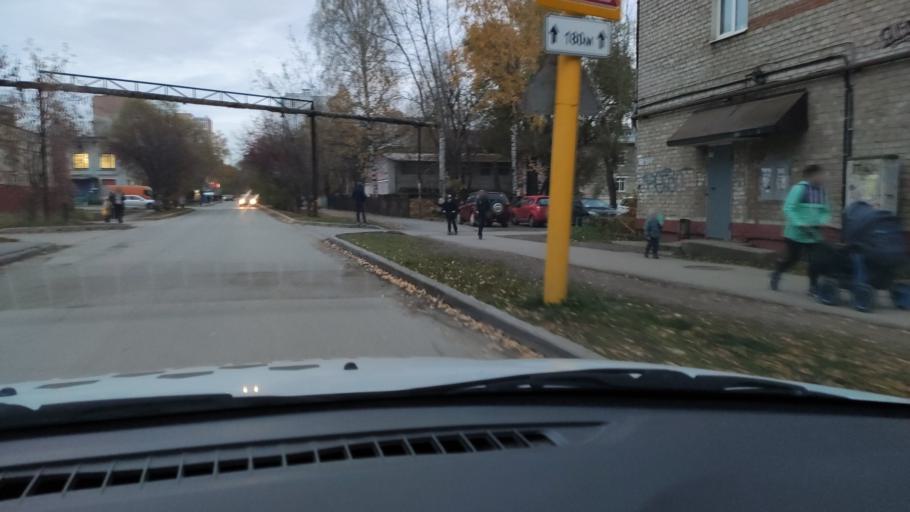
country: RU
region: Perm
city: Kondratovo
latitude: 58.0384
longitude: 56.1253
